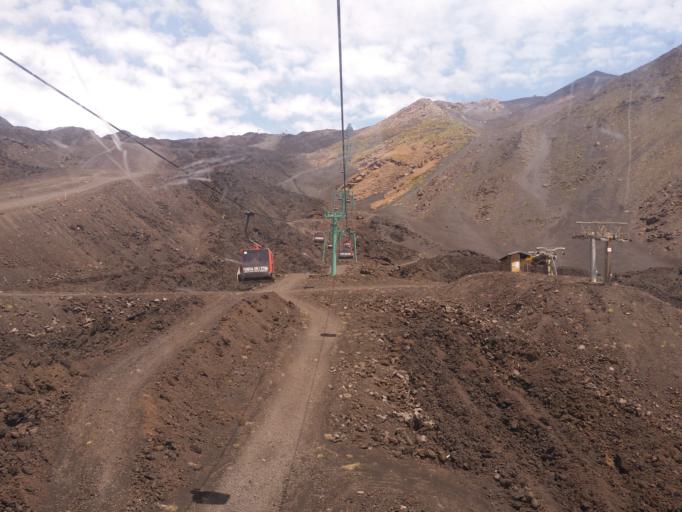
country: IT
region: Sicily
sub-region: Catania
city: Ragalna
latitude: 37.7078
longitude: 14.9994
